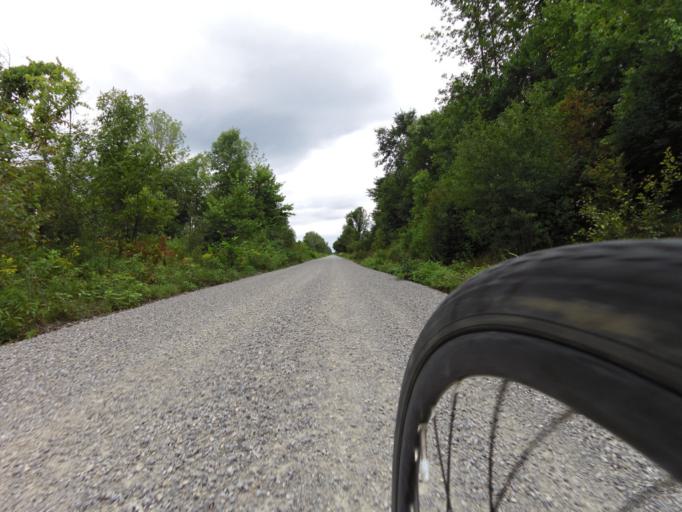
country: CA
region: Ontario
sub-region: Lanark County
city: Smiths Falls
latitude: 44.9304
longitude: -76.0342
